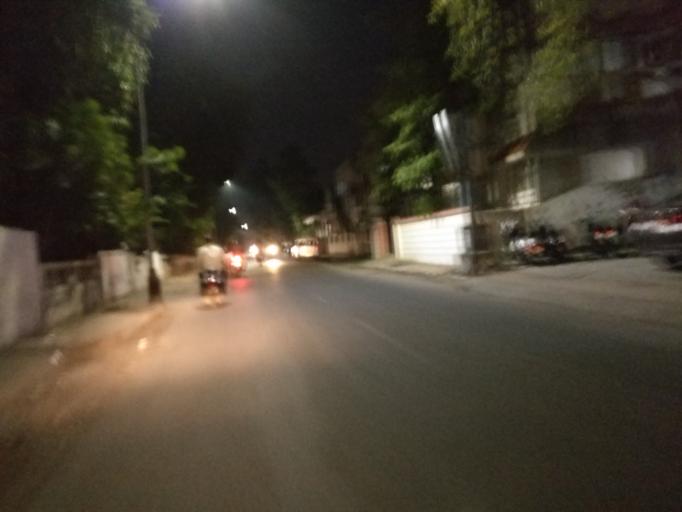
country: IN
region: Gujarat
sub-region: Ahmadabad
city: Ahmedabad
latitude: 23.0008
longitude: 72.5603
